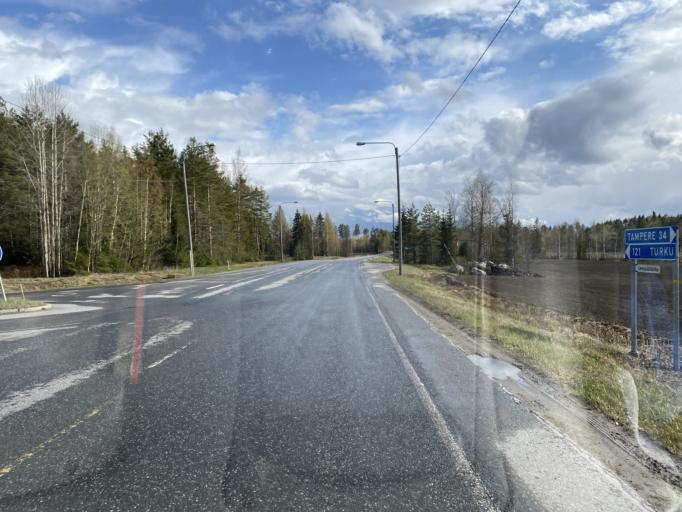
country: FI
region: Pirkanmaa
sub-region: Etelae-Pirkanmaa
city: Viiala
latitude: 61.2033
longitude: 23.7348
